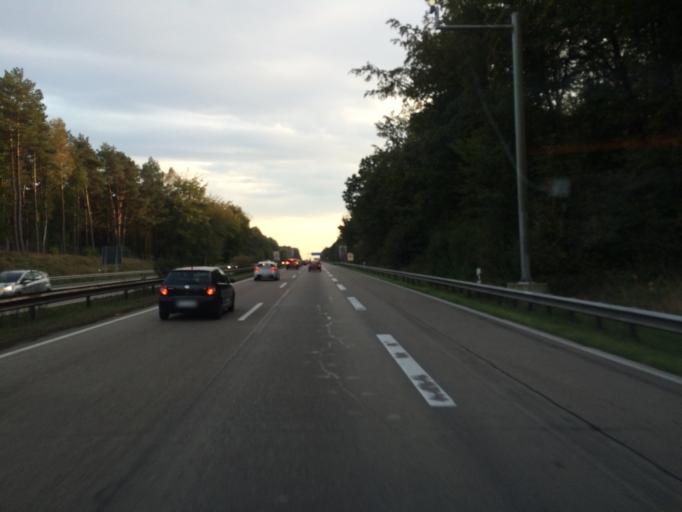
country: DE
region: Lower Saxony
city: Bad Fallingbostel
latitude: 52.8070
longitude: 9.6786
